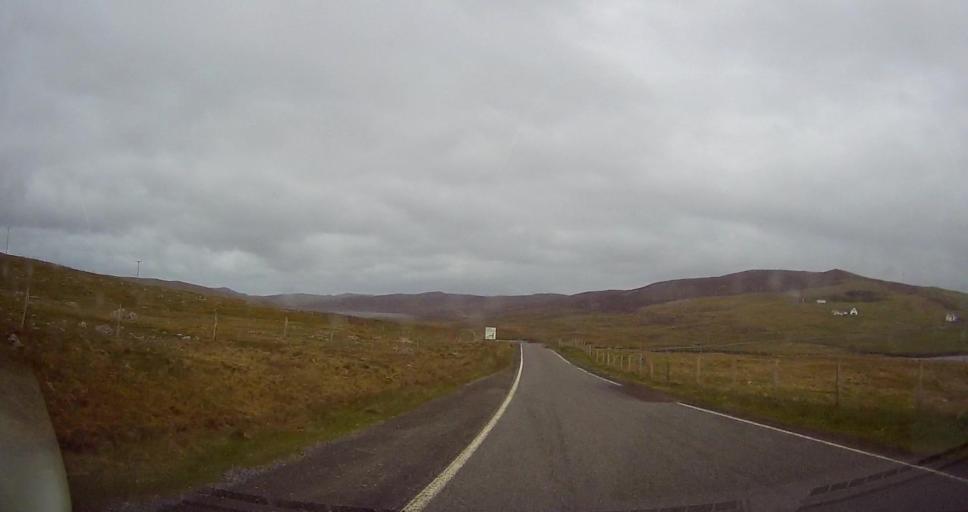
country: GB
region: Scotland
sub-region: Shetland Islands
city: Sandwick
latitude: 60.2410
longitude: -1.5345
